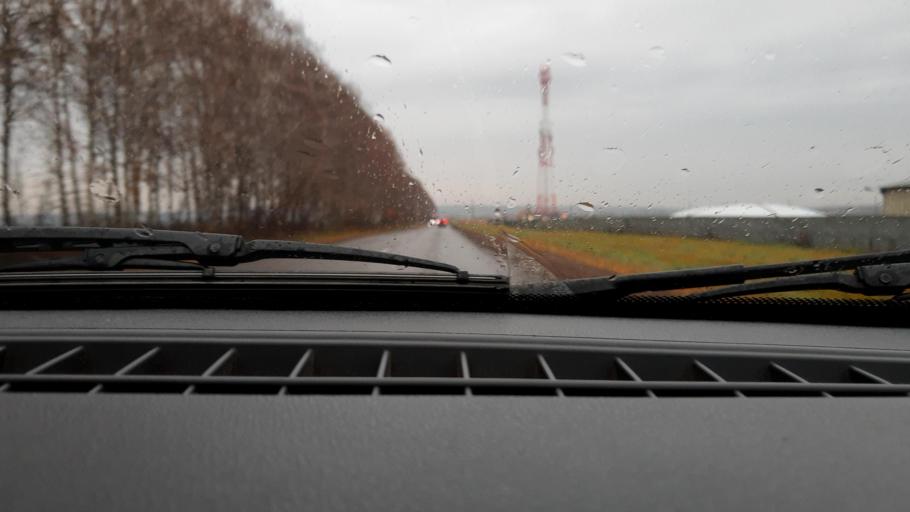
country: RU
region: Bashkortostan
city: Ufa
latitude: 54.8247
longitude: 55.9839
